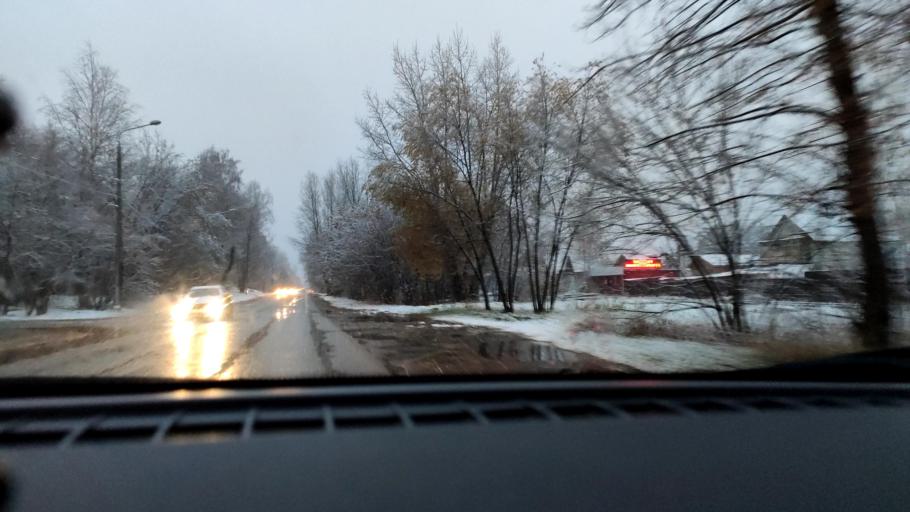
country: RU
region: Perm
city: Overyata
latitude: 58.0095
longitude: 55.9484
